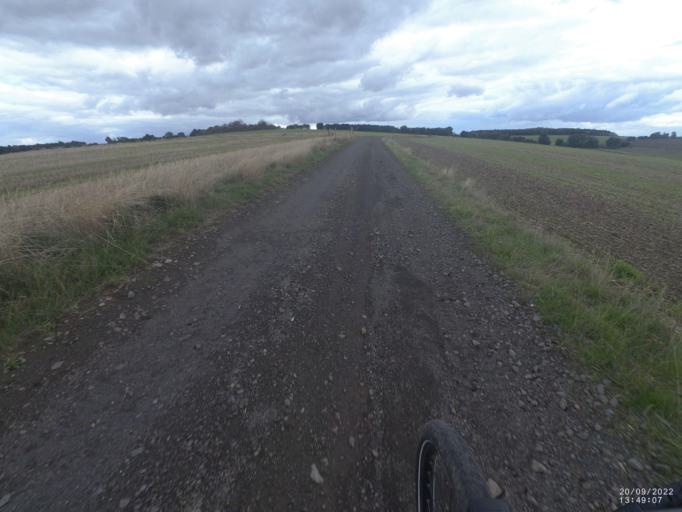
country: DE
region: Rheinland-Pfalz
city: Strohn
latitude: 50.1173
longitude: 6.9318
